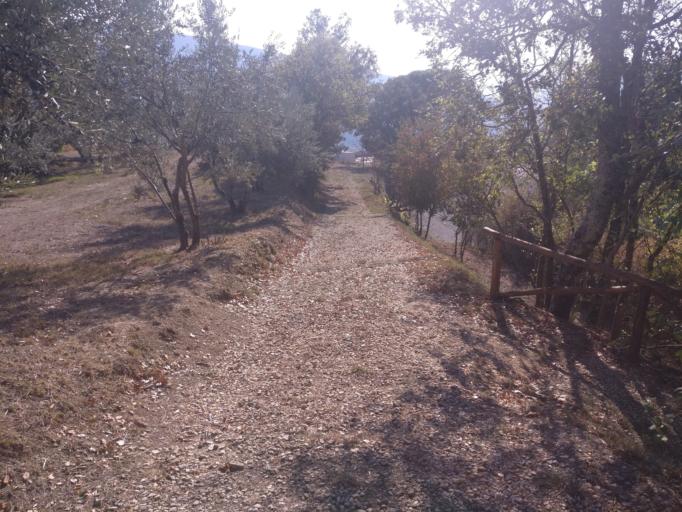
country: IT
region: Tuscany
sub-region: Province of Florence
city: Londa
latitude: 43.8739
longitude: 11.5493
